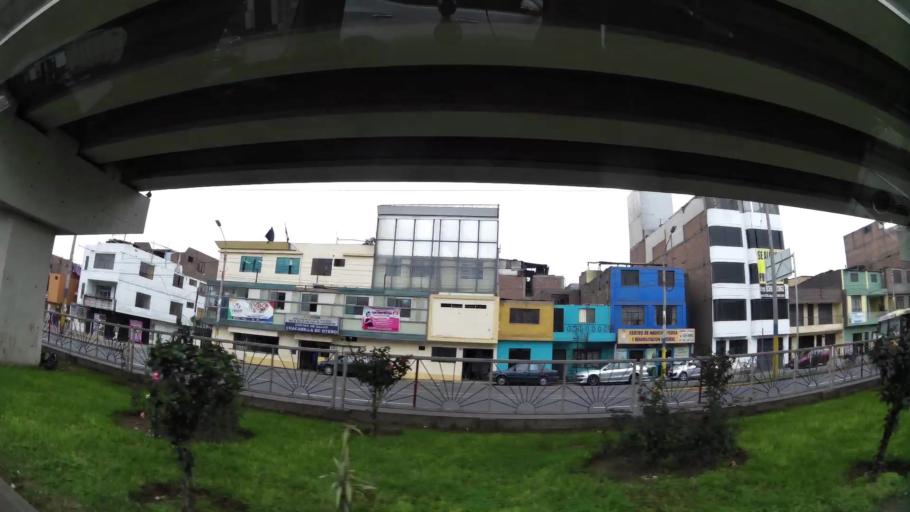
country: PE
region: Lima
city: Lima
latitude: -12.0253
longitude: -77.0092
